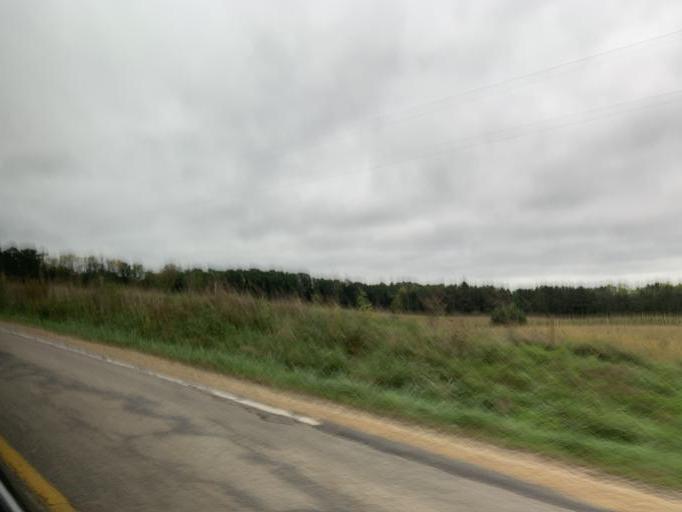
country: US
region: Wisconsin
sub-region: Grant County
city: Muscoda
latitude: 43.2052
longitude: -90.4074
